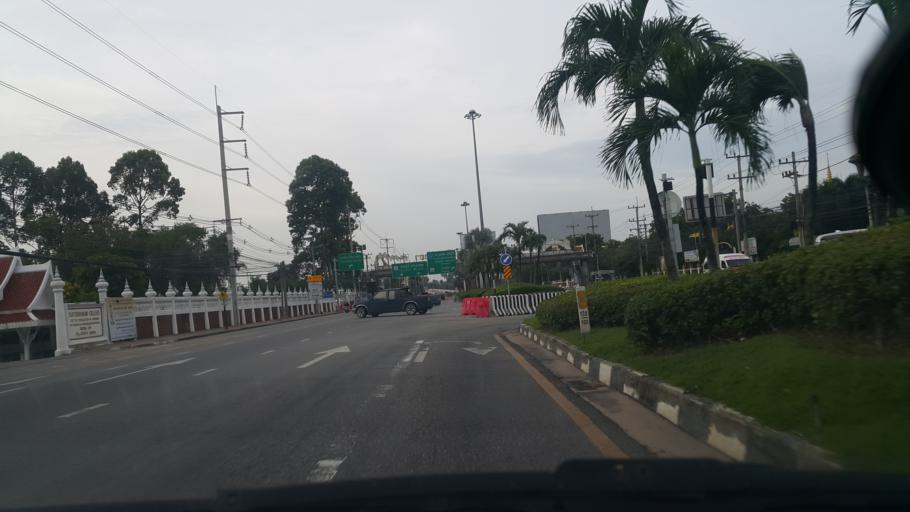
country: TH
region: Chon Buri
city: Bang Lamung
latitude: 12.9942
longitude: 100.9269
